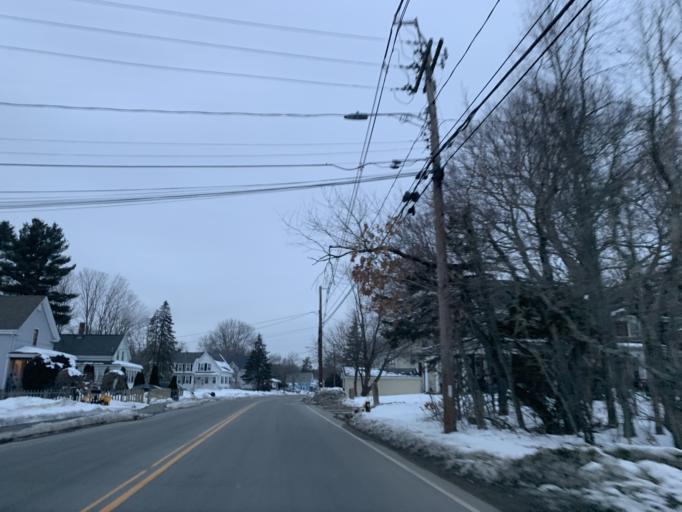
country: US
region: Massachusetts
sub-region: Norfolk County
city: Stoughton
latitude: 42.1313
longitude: -71.1084
